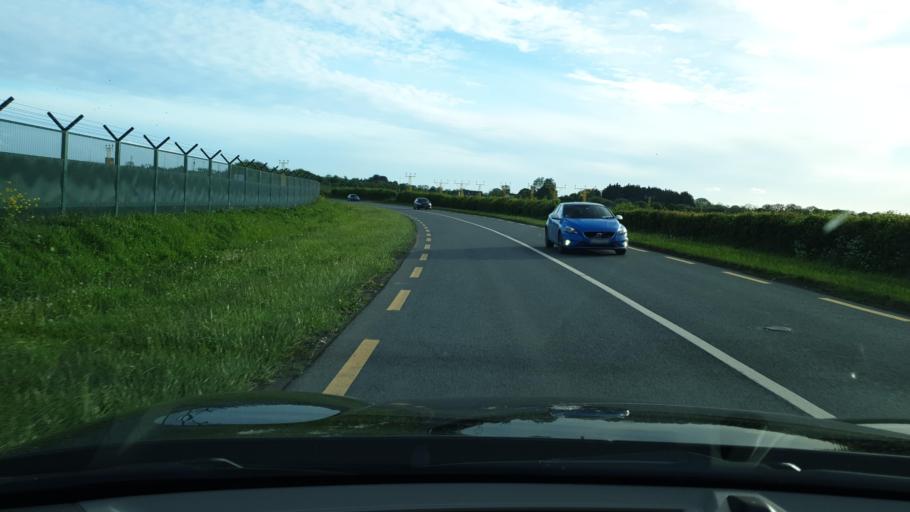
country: IE
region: Leinster
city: Ballymun
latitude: 53.4379
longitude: -6.2892
